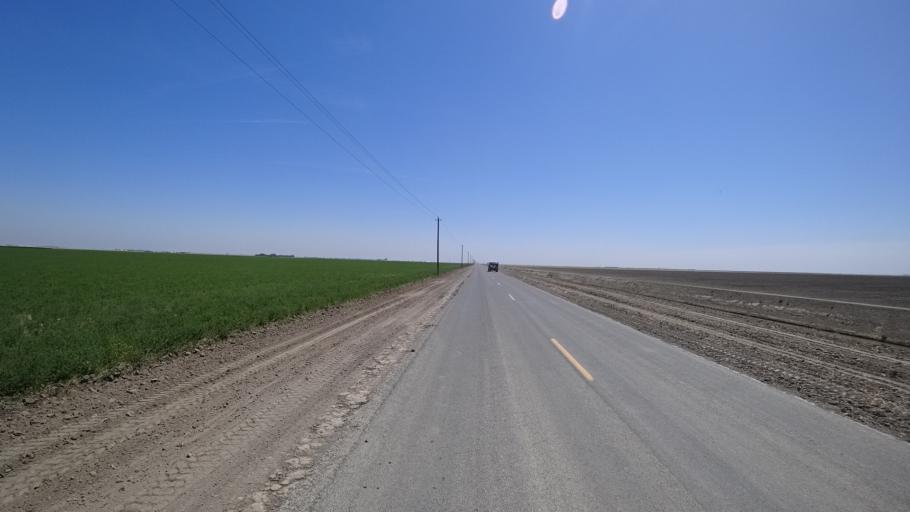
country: US
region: California
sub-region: Kings County
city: Corcoran
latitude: 36.0215
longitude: -119.5953
